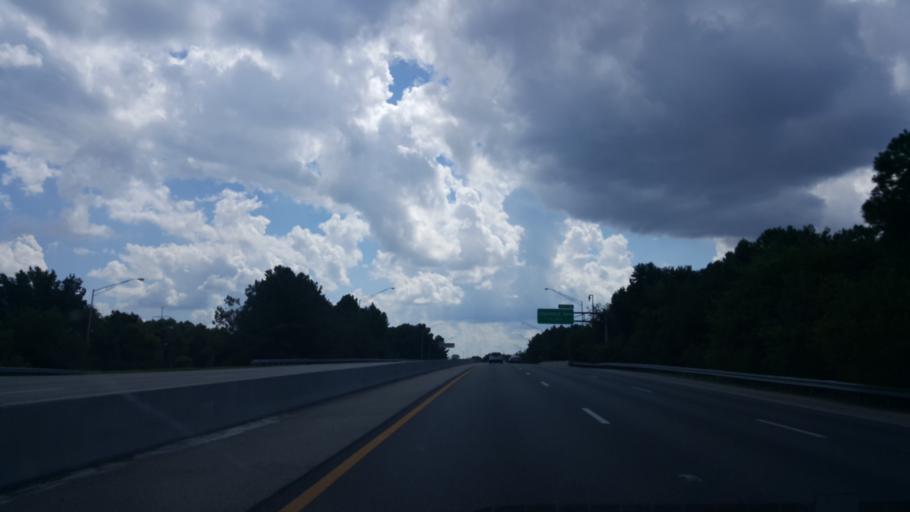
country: US
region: Virginia
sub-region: City of Newport News
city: Newport News
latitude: 37.0052
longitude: -76.4019
